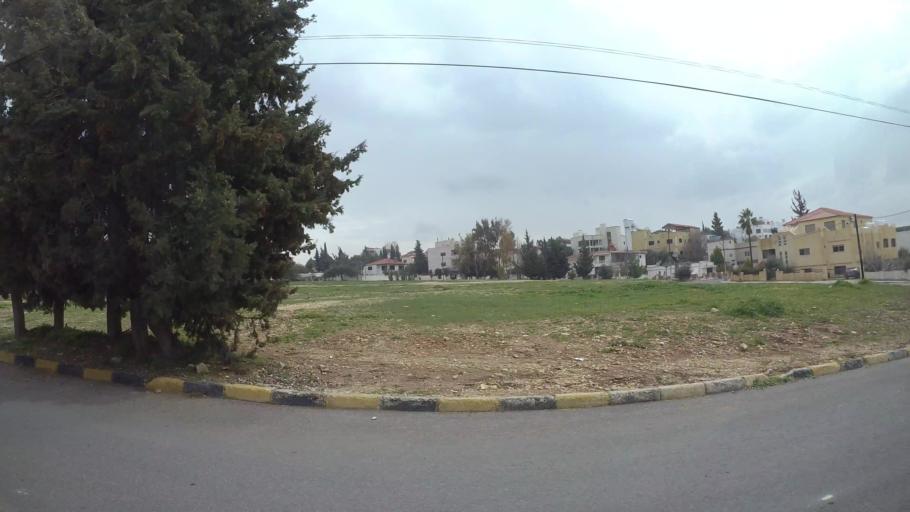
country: JO
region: Amman
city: Umm as Summaq
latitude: 31.8937
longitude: 35.8570
